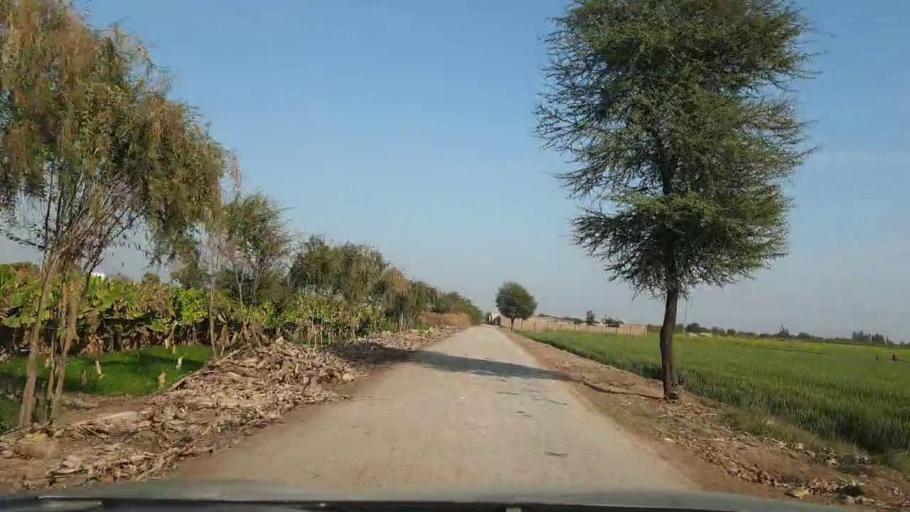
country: PK
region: Sindh
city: Berani
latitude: 25.7270
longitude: 68.7814
